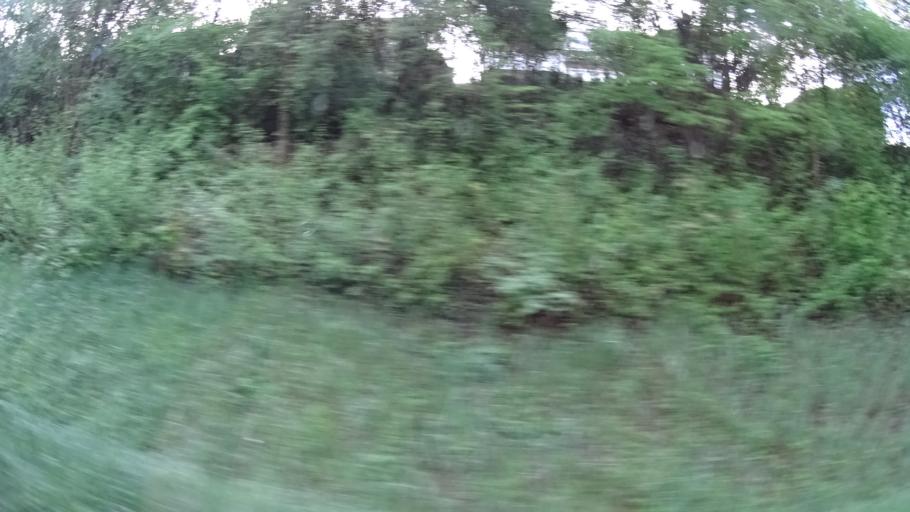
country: DE
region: Baden-Wuerttemberg
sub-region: Karlsruhe Region
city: Empfingen
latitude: 48.4227
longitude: 8.7651
